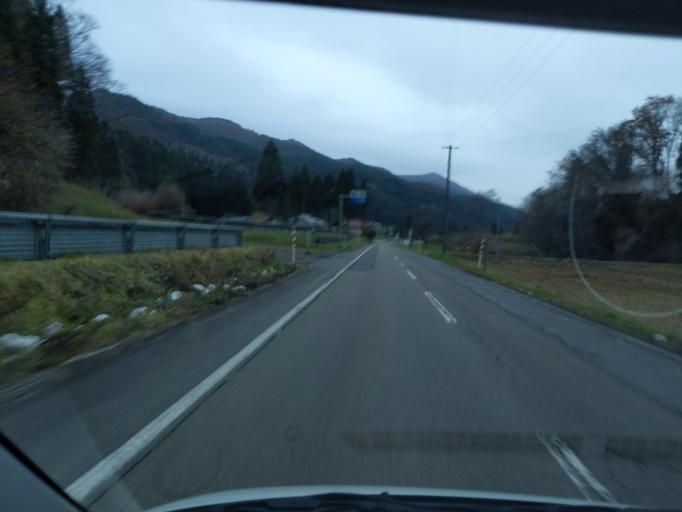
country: JP
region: Iwate
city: Tono
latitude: 39.1275
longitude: 141.3804
